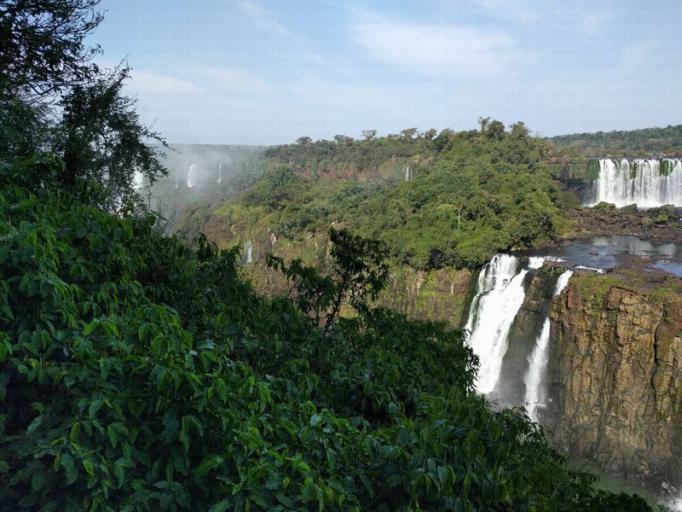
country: AR
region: Misiones
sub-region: Departamento de Iguazu
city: Puerto Iguazu
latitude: -25.6884
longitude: -54.4396
